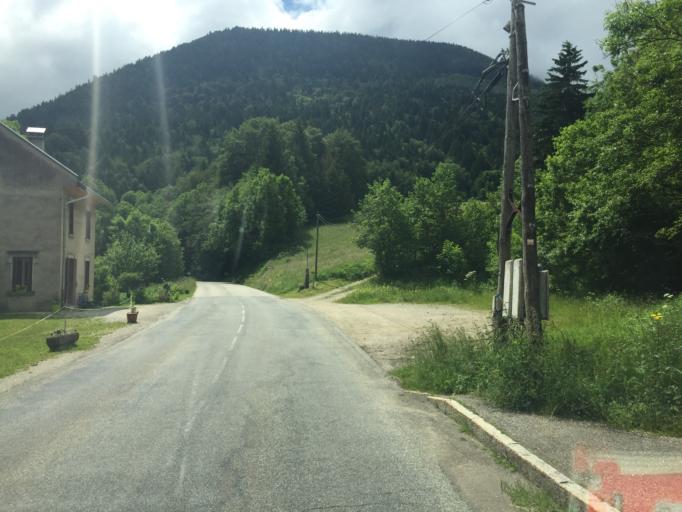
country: FR
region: Rhone-Alpes
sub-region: Departement de la Savoie
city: Cruet
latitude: 45.6170
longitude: 6.0825
